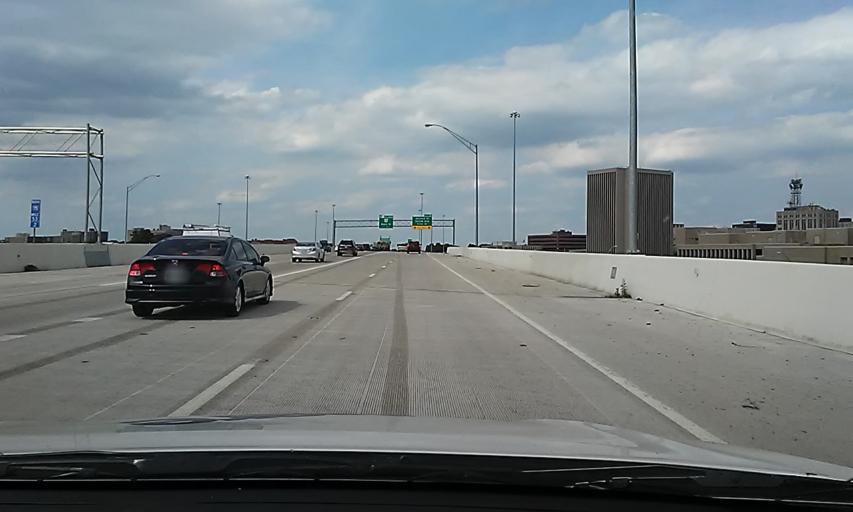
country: US
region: Ohio
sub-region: Montgomery County
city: Dayton
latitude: 39.7557
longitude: -84.2032
